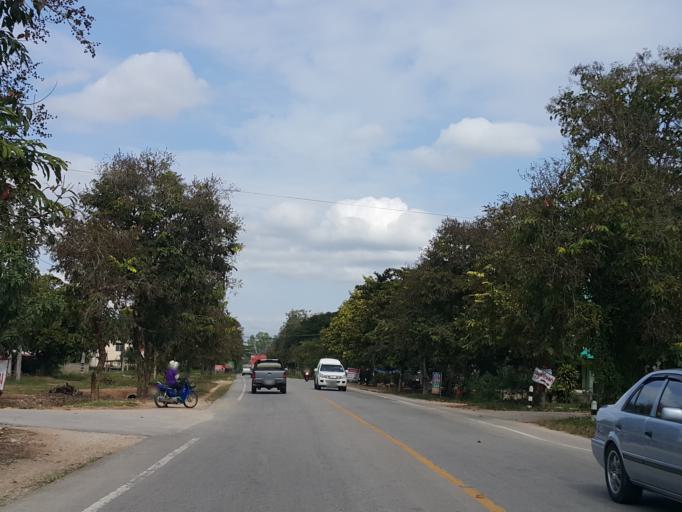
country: TH
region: Lampang
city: Lampang
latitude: 18.3483
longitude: 99.4594
